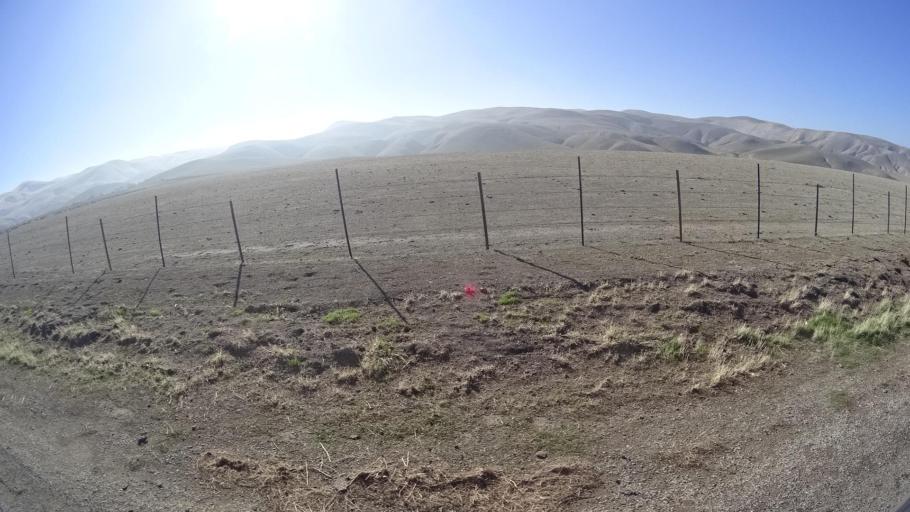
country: US
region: California
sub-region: Kern County
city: Maricopa
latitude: 34.9956
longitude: -119.3959
